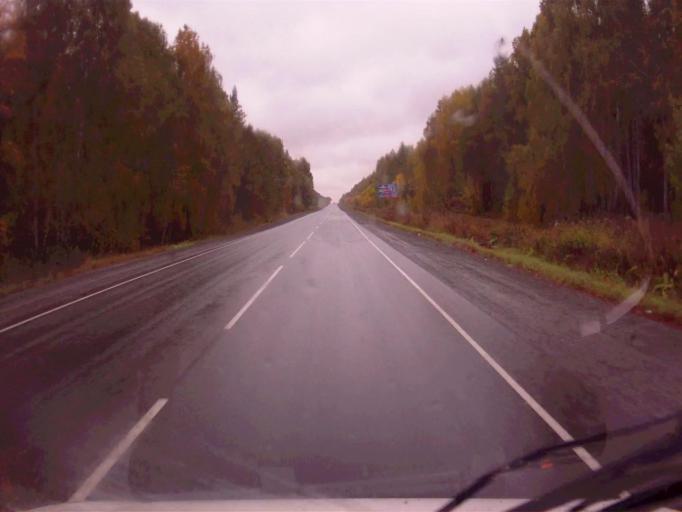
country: RU
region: Chelyabinsk
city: Roshchino
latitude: 55.3728
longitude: 61.1558
